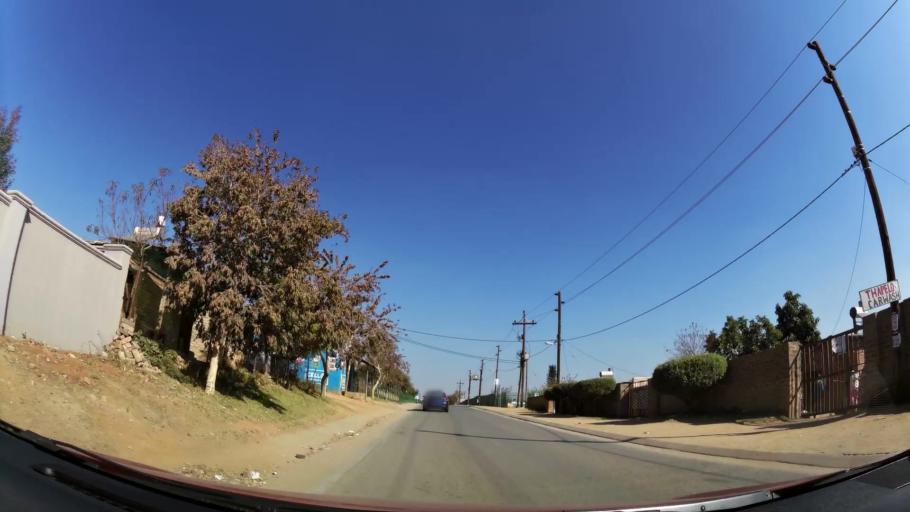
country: ZA
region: Gauteng
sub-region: West Rand District Municipality
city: Muldersdriseloop
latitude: -26.0216
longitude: 27.9207
